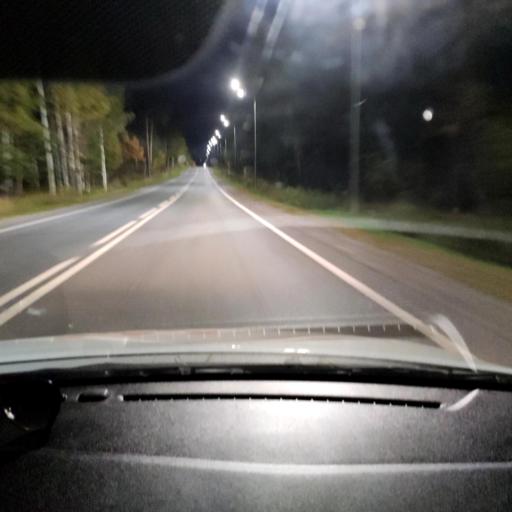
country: RU
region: Tatarstan
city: Stolbishchi
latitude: 55.6344
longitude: 49.0856
